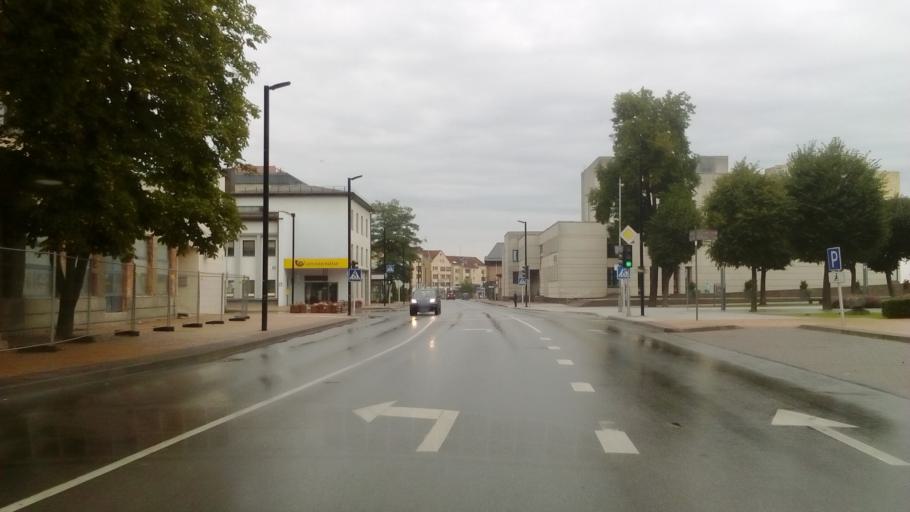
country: LT
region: Alytaus apskritis
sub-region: Alytus
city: Alytus
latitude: 54.3954
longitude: 24.0459
